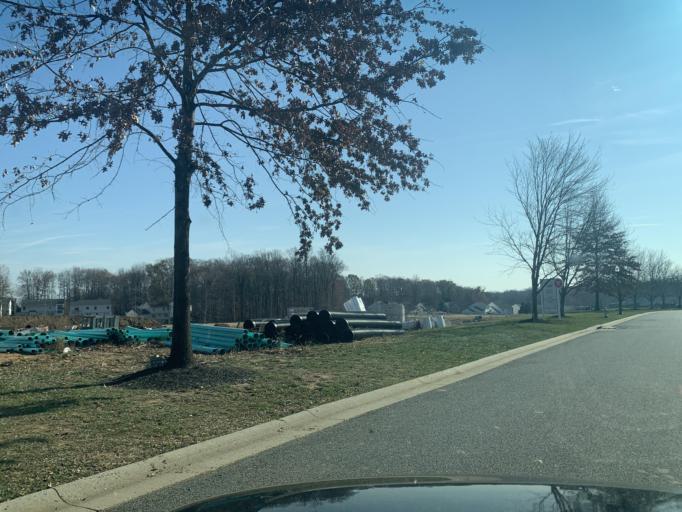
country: US
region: Maryland
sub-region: Harford County
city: Havre de Grace
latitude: 39.5479
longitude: -76.1201
